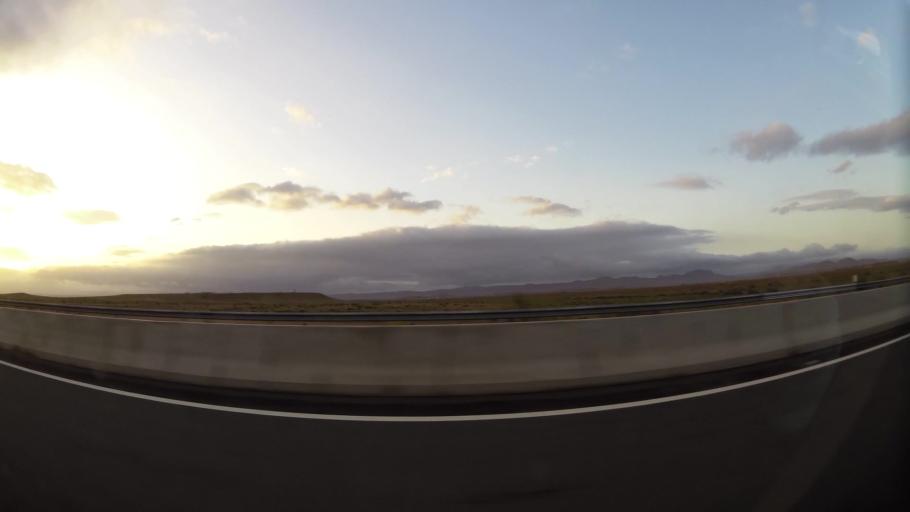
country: MA
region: Oriental
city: Taourirt
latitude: 34.5488
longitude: -2.8875
